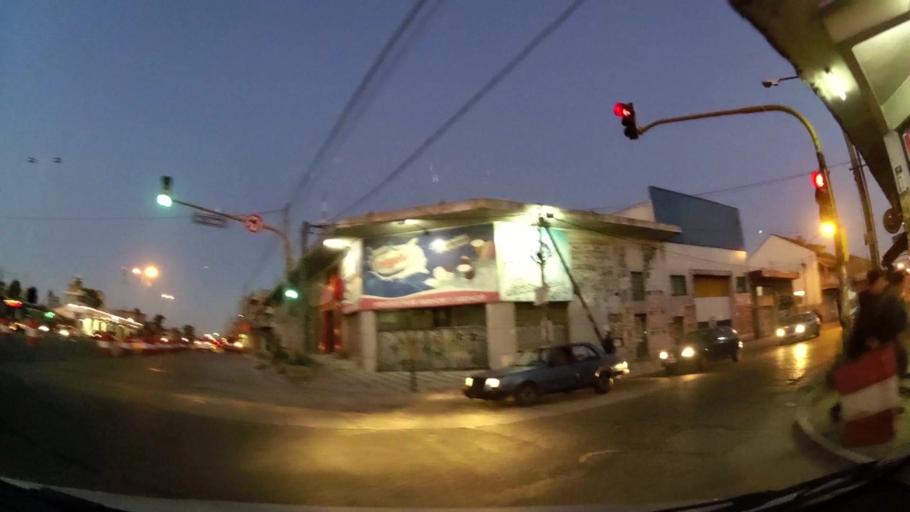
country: AR
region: Buenos Aires
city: San Justo
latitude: -34.7085
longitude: -58.5868
